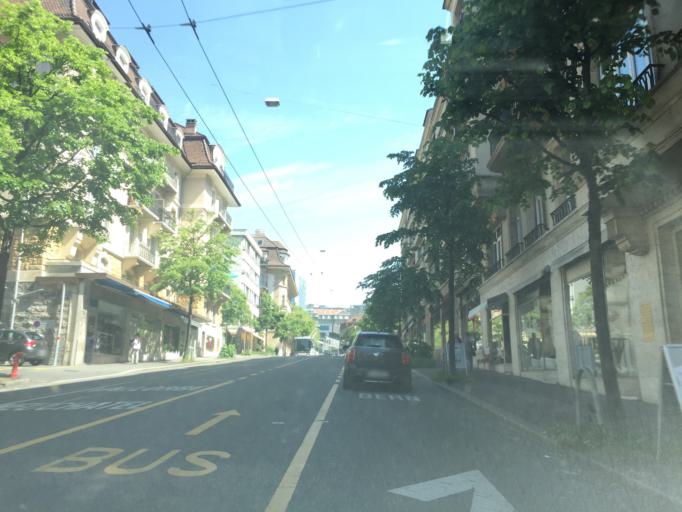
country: CH
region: Vaud
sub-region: Lausanne District
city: Lausanne
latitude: 46.5155
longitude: 6.6371
